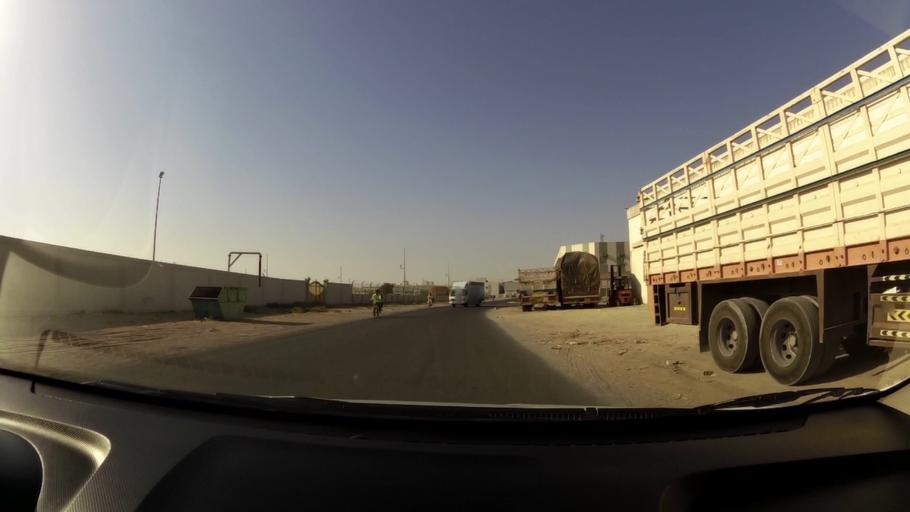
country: AE
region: Ajman
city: Ajman
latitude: 25.4386
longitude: 55.5435
